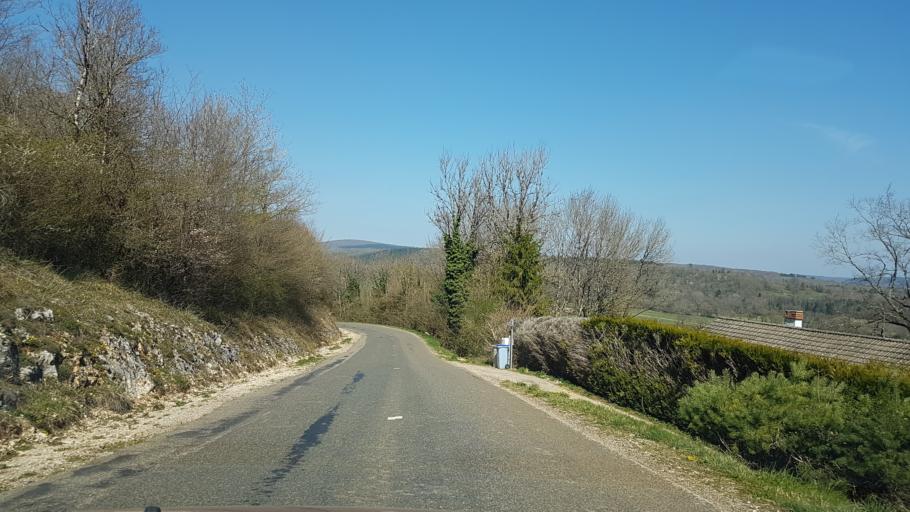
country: FR
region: Franche-Comte
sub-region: Departement du Jura
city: Orgelet
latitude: 46.5250
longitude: 5.5442
